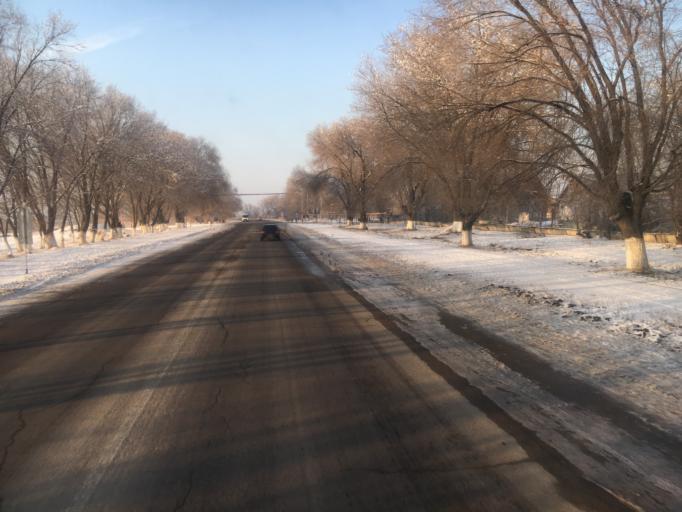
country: KZ
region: Almaty Oblysy
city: Burunday
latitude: 43.3383
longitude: 76.6594
